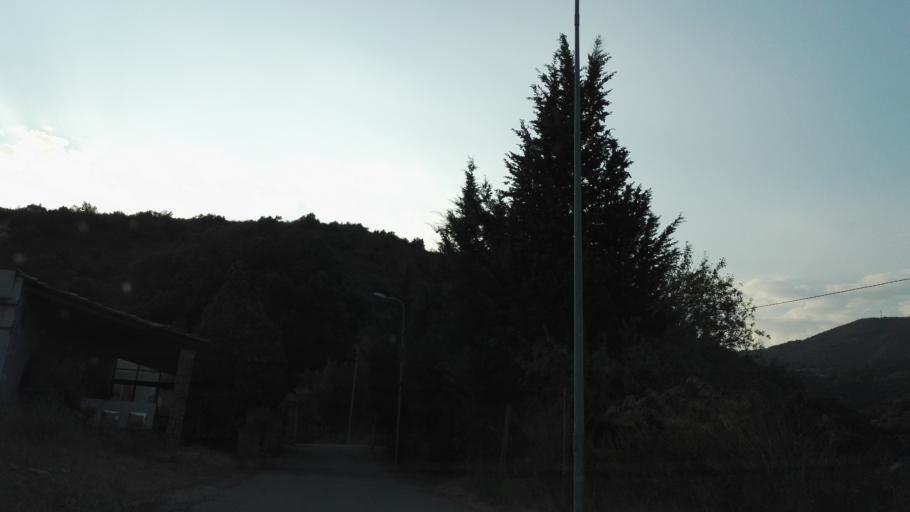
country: IT
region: Calabria
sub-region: Provincia di Reggio Calabria
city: Placanica
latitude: 38.4066
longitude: 16.4255
